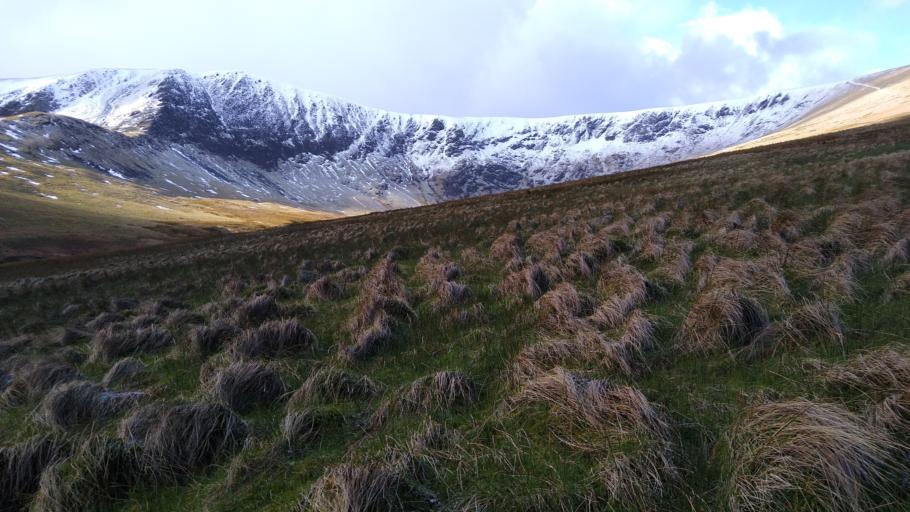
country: GB
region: England
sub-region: Cumbria
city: Keswick
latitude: 54.6581
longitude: -3.0121
